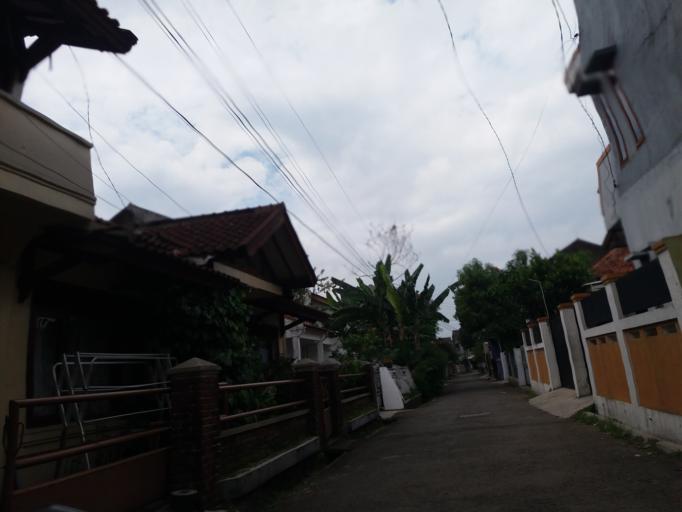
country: ID
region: West Java
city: Bandung
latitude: -6.9247
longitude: 107.6514
